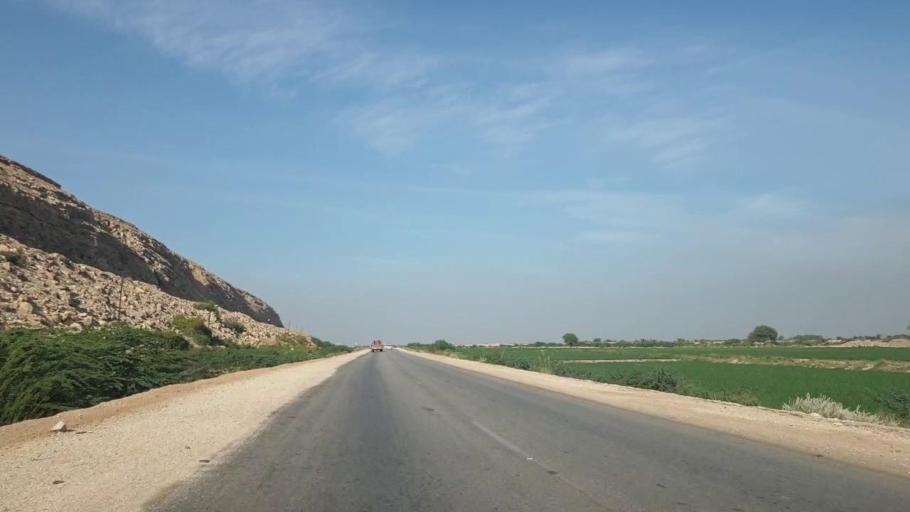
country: PK
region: Sindh
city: Sehwan
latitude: 26.3591
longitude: 67.8733
